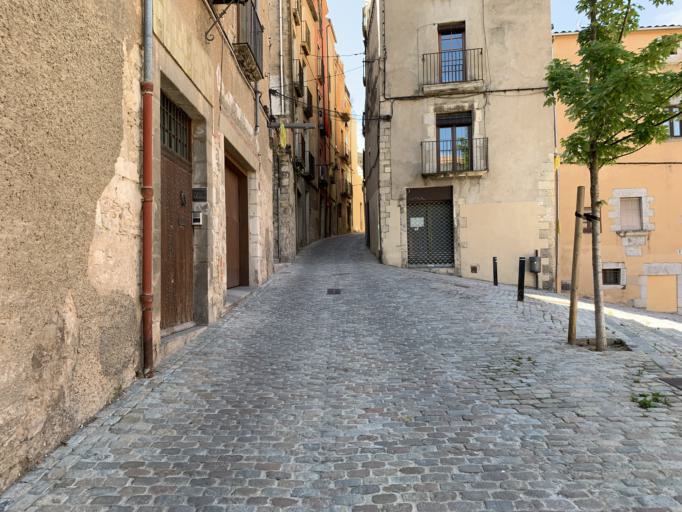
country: ES
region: Catalonia
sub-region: Provincia de Girona
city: Girona
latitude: 41.9831
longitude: 2.8259
